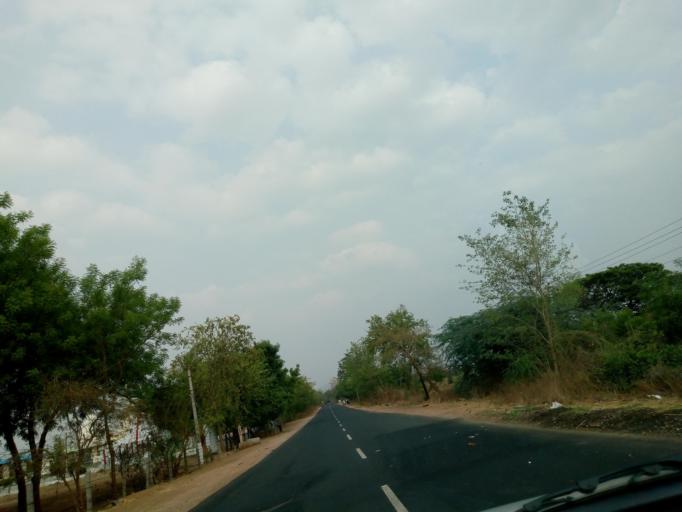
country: IN
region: Andhra Pradesh
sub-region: Prakasam
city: Diguvametta
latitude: 15.3785
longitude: 78.8664
